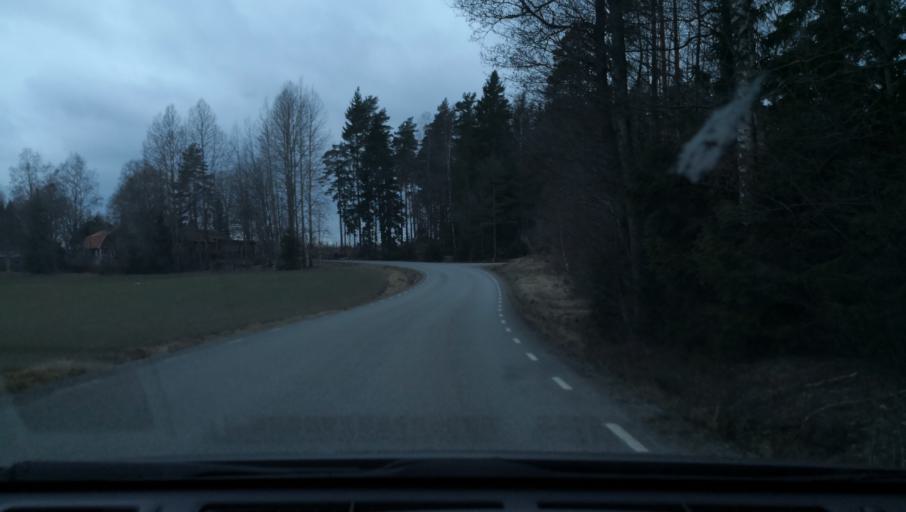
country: SE
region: Vaestmanland
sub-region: Kopings Kommun
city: Kolsva
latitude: 59.5673
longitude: 15.7653
